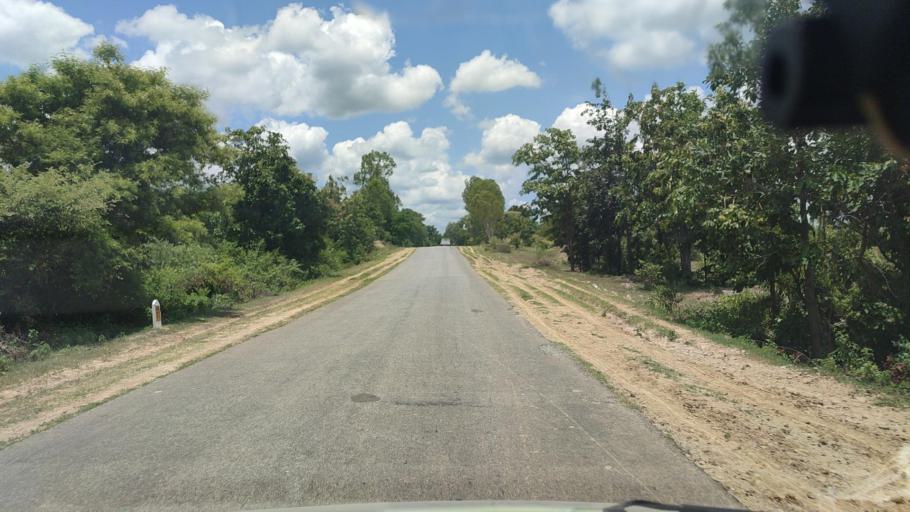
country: MM
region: Magway
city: Taungdwingyi
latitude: 20.1573
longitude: 95.6086
